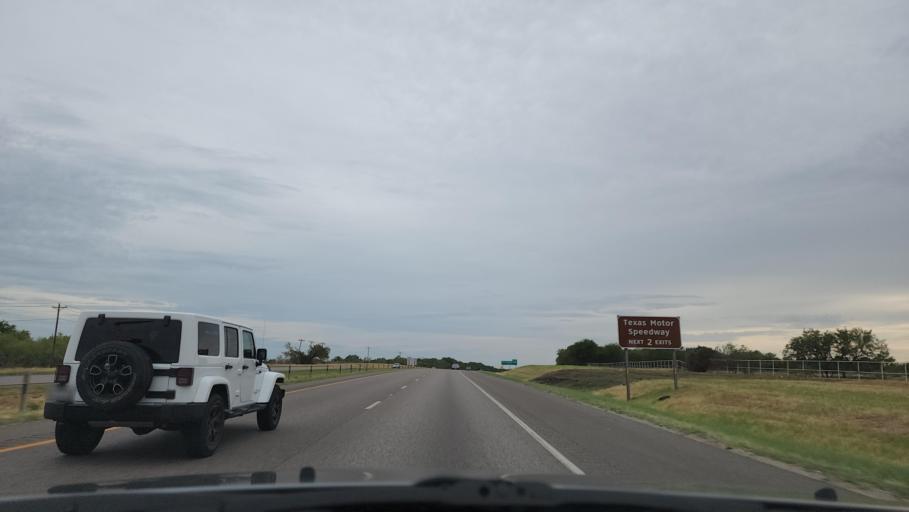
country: US
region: Texas
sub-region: Denton County
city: Justin
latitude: 33.0574
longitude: -97.2478
